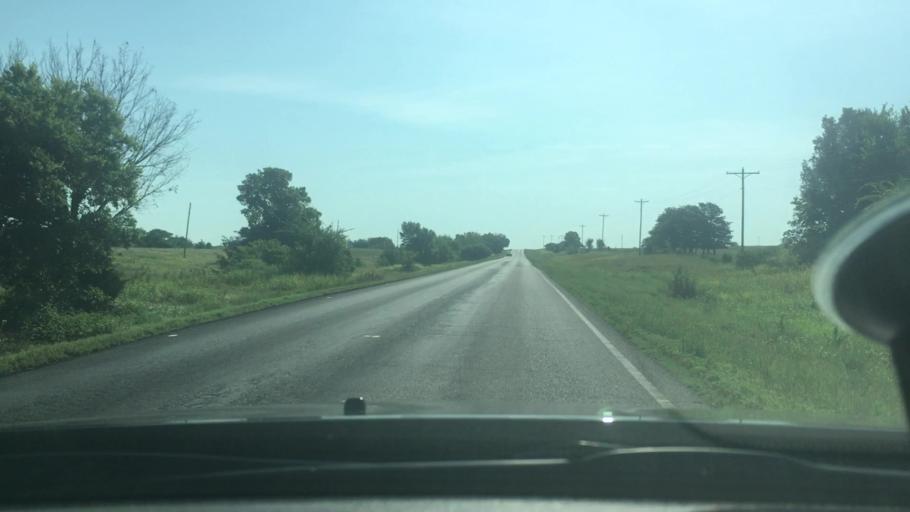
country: US
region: Oklahoma
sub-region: Garvin County
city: Pauls Valley
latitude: 34.6519
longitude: -97.2898
